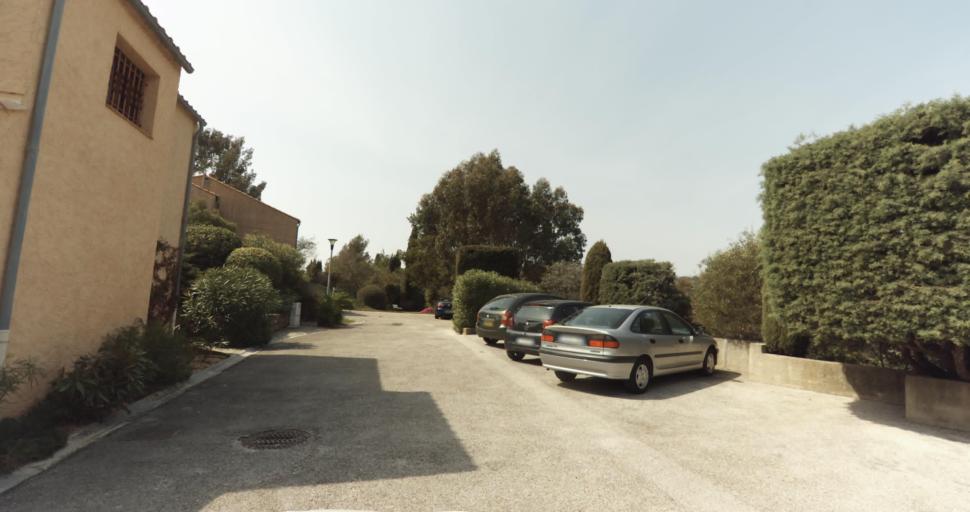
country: FR
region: Provence-Alpes-Cote d'Azur
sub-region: Departement du Var
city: Bormes-les-Mimosas
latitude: 43.1468
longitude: 6.3502
